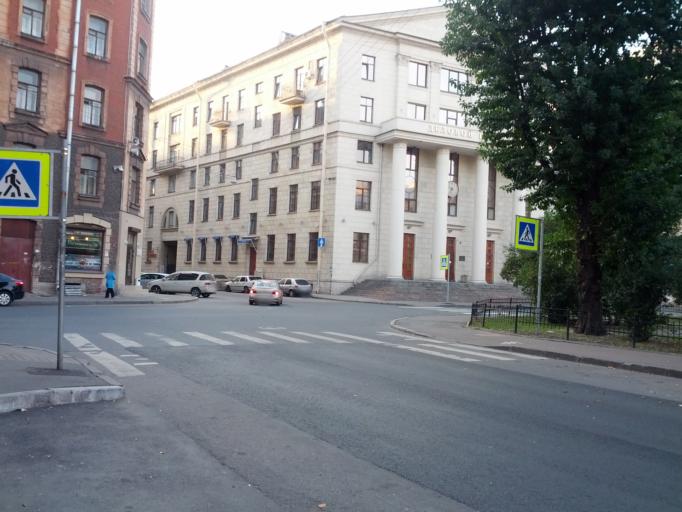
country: RU
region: St.-Petersburg
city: Saint Petersburg
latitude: 59.9508
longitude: 30.3035
